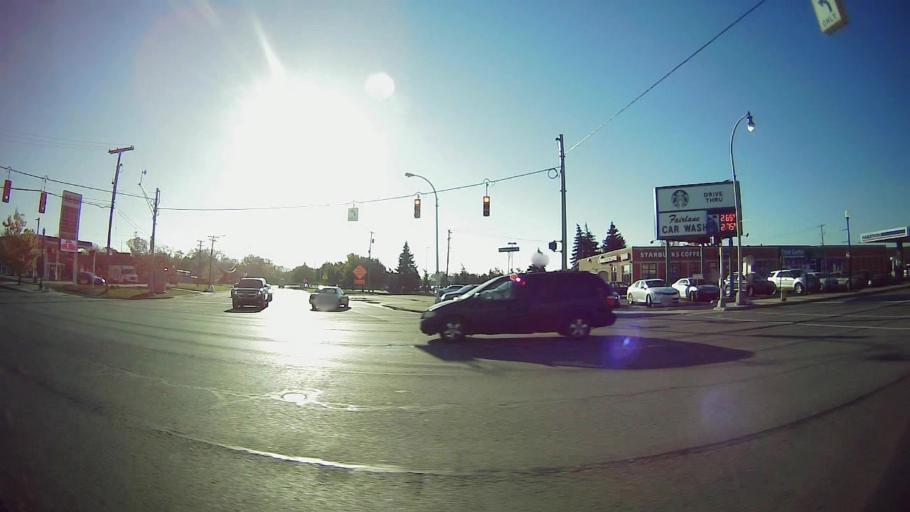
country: US
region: Michigan
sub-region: Wayne County
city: Dearborn
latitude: 42.3244
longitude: -83.1684
